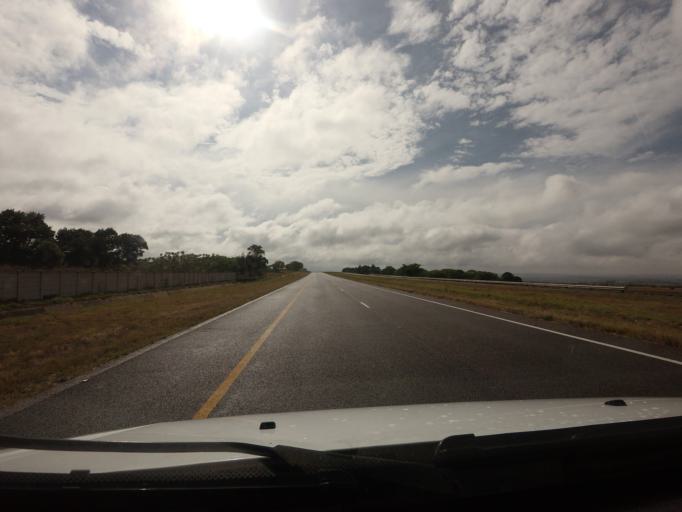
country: ZA
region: Gauteng
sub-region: City of Tshwane Metropolitan Municipality
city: Cullinan
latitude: -25.7985
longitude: 28.5824
